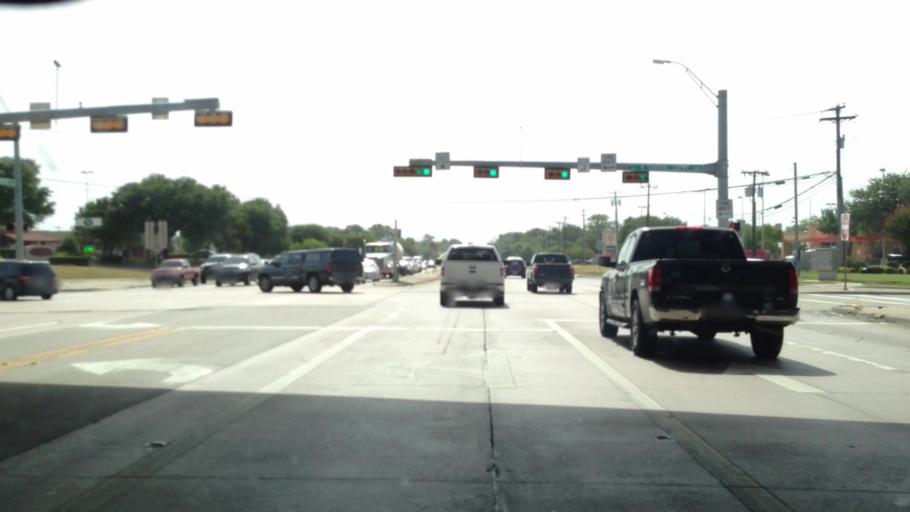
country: US
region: Texas
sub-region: Collin County
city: McKinney
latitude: 33.2168
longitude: -96.6364
